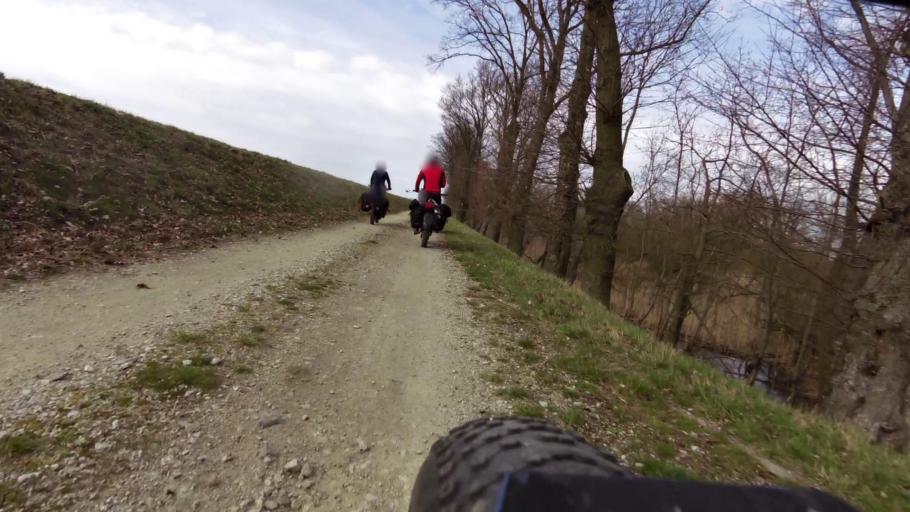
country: DE
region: Brandenburg
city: Reitwein
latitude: 52.5130
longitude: 14.6148
